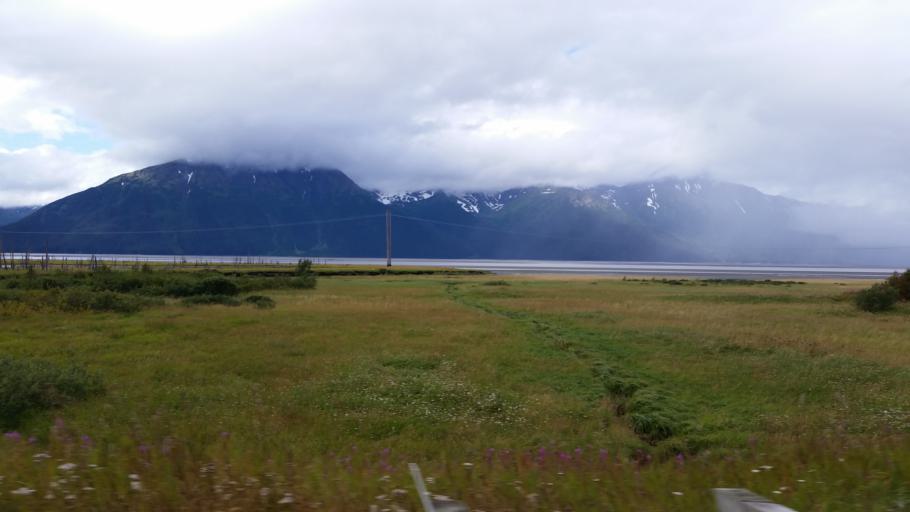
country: US
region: Alaska
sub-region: Anchorage Municipality
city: Girdwood
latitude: 60.9393
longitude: -149.1698
